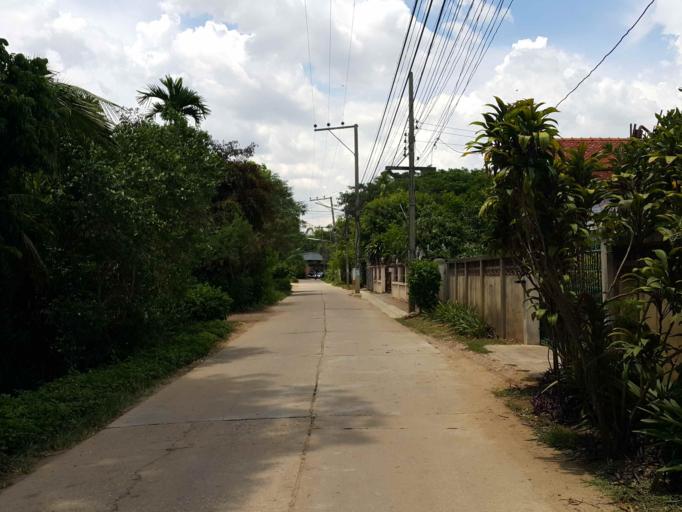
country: TH
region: Chiang Mai
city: Chiang Mai
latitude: 18.7469
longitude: 98.9888
